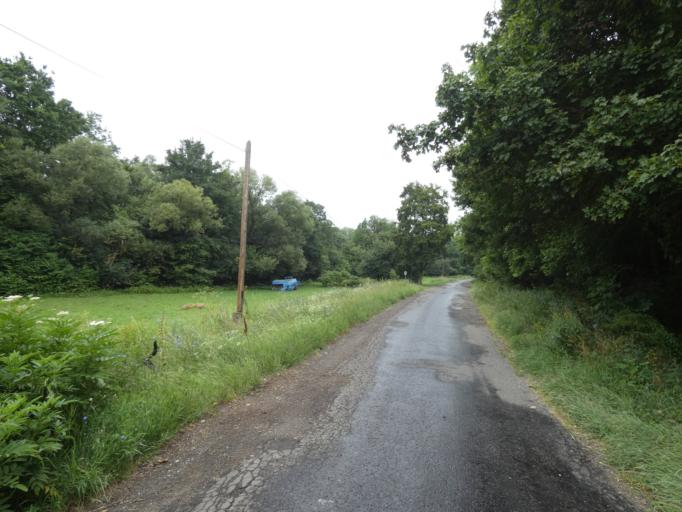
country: HU
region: Pest
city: Szob
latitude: 47.8175
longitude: 18.8974
